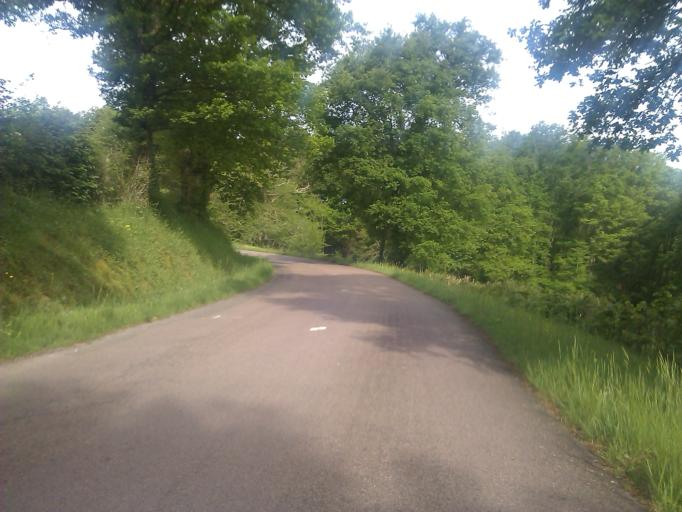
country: FR
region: Auvergne
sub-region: Departement de l'Allier
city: Cerilly
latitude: 46.6156
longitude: 2.7615
